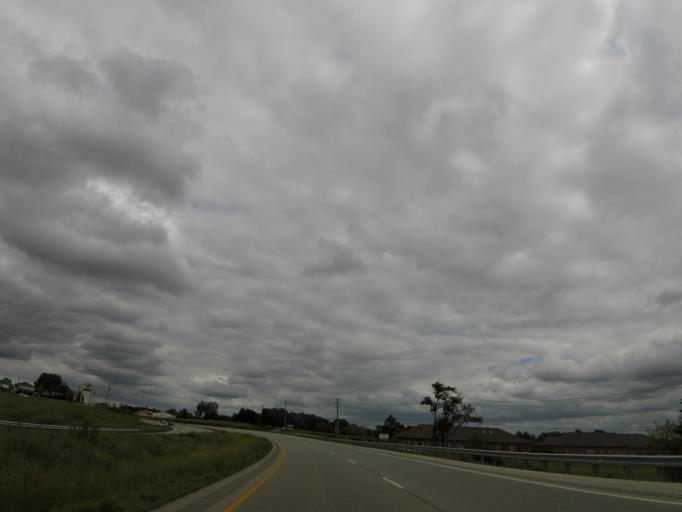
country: US
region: Kentucky
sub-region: Scott County
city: Georgetown
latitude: 38.1836
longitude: -84.5685
